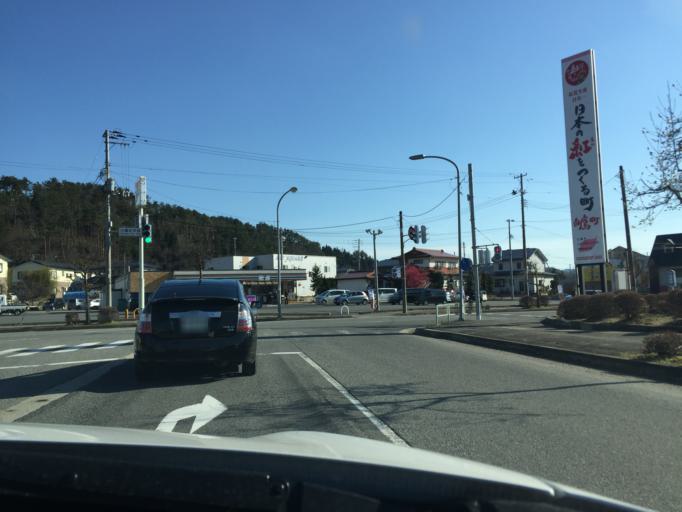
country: JP
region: Yamagata
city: Nagai
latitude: 38.1816
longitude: 140.1018
